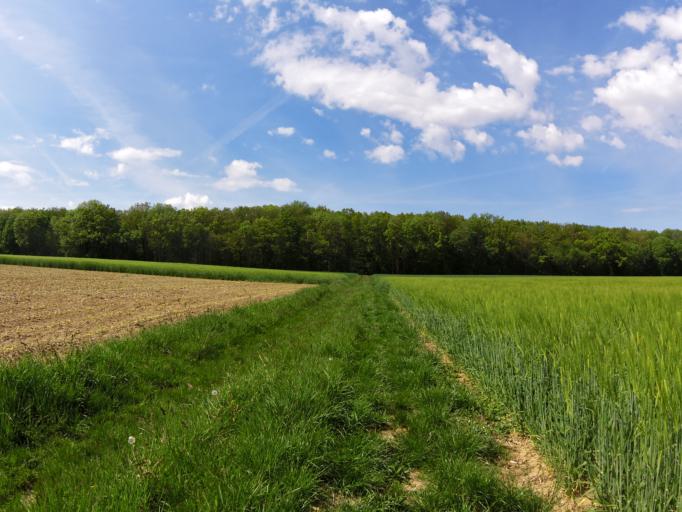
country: DE
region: Bavaria
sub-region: Regierungsbezirk Unterfranken
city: Theilheim
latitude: 49.7401
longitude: 10.0322
